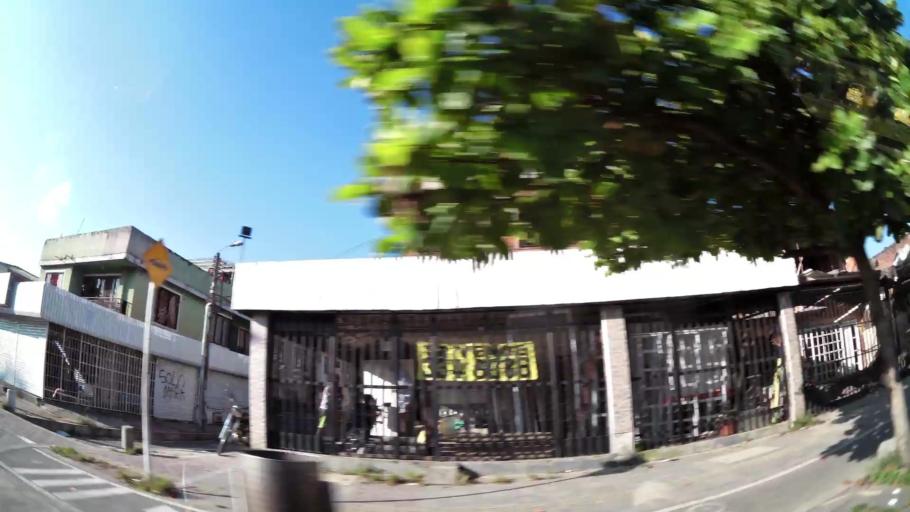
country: CO
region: Valle del Cauca
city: Cali
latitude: 3.4342
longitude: -76.5135
